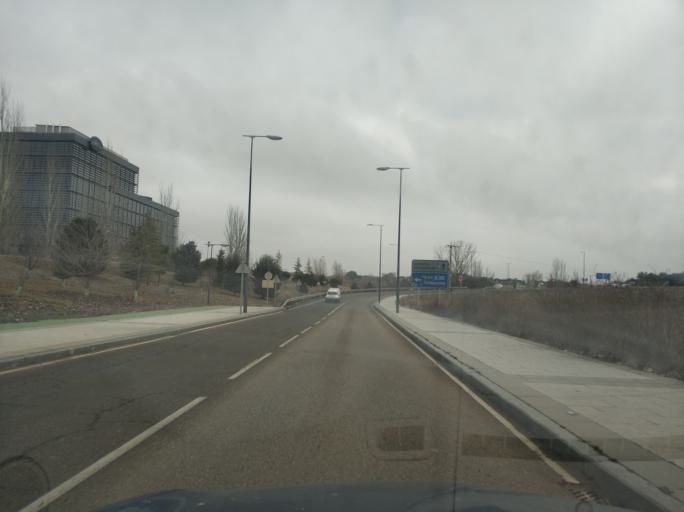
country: ES
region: Castille and Leon
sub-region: Provincia de Valladolid
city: Arroyo
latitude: 41.6133
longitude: -4.7980
